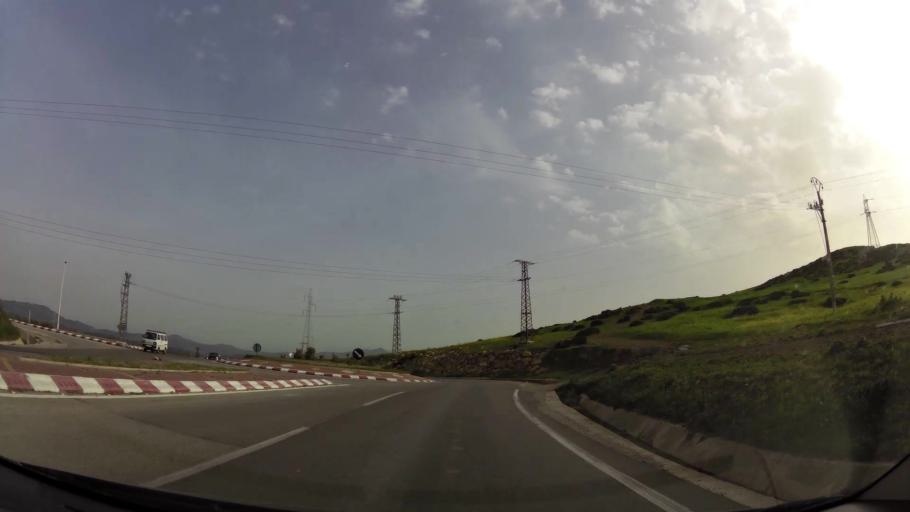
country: MA
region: Tanger-Tetouan
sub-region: Tanger-Assilah
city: Dar Chaoui
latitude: 35.6375
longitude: -5.6838
